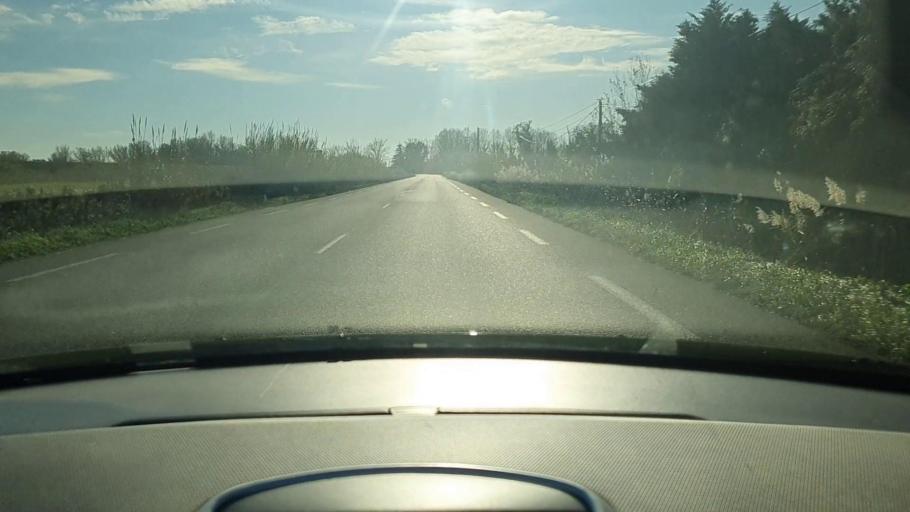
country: FR
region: Languedoc-Roussillon
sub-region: Departement du Gard
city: Fourques
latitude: 43.7280
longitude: 4.6080
